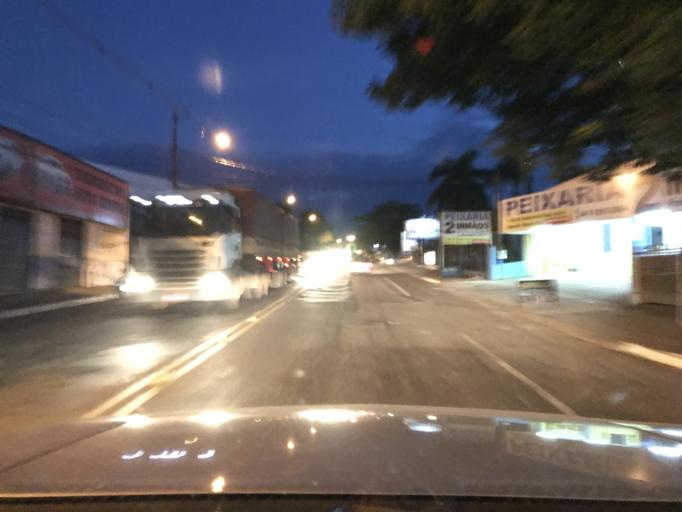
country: PY
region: Canindeyu
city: Salto del Guaira
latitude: -24.0805
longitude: -54.2435
